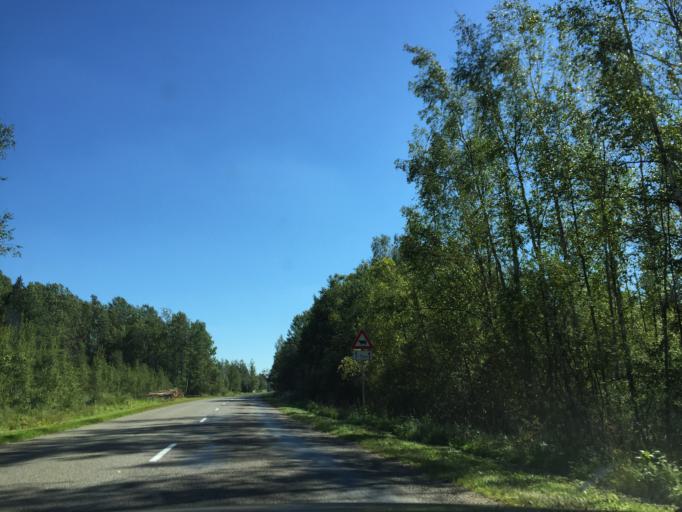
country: LV
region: Akniste
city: Akniste
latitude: 56.0723
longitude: 25.8886
